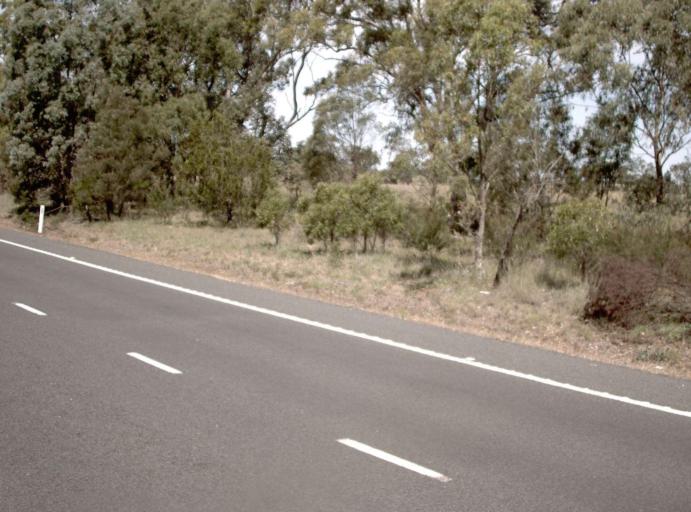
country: AU
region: Victoria
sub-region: Wellington
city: Sale
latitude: -37.9369
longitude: 147.1598
